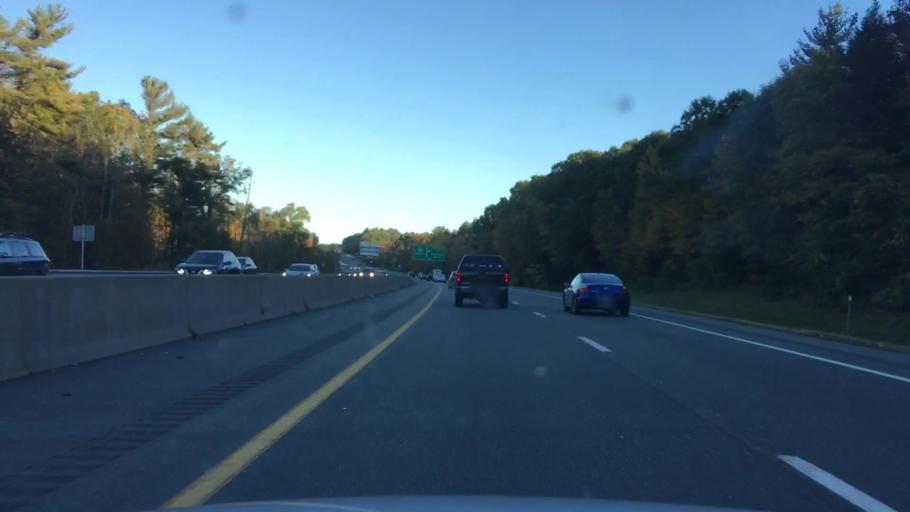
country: US
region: New Hampshire
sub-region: Rockingham County
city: Hampton
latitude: 42.9662
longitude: -70.8838
